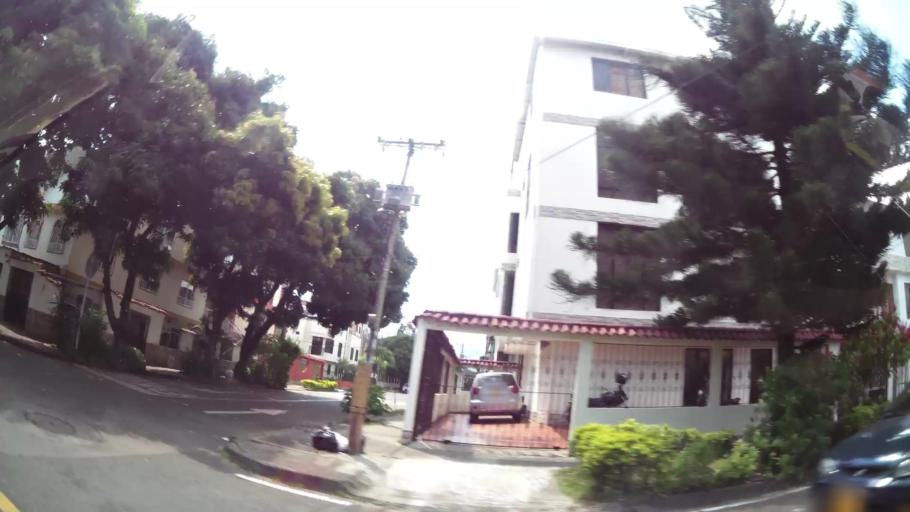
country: CO
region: Valle del Cauca
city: Cali
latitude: 3.4070
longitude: -76.5322
